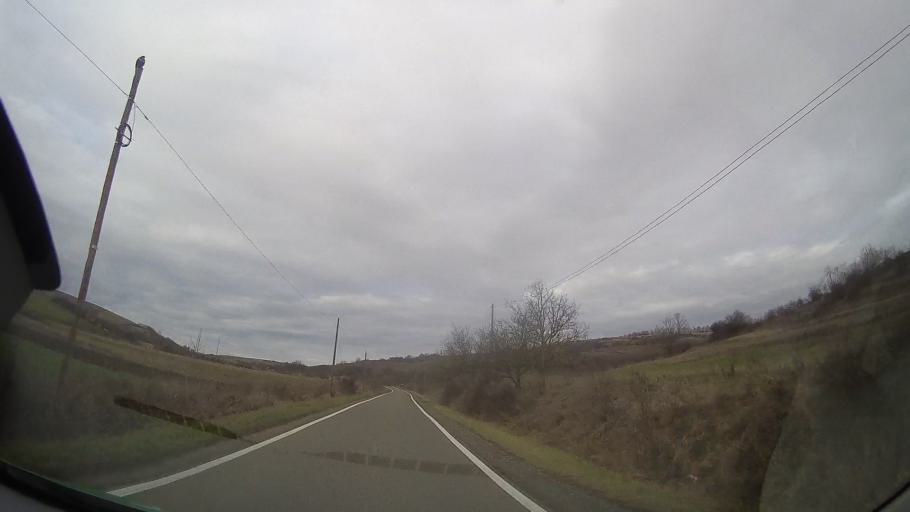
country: RO
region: Mures
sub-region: Comuna Cozma
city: Cozma
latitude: 46.8009
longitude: 24.5358
